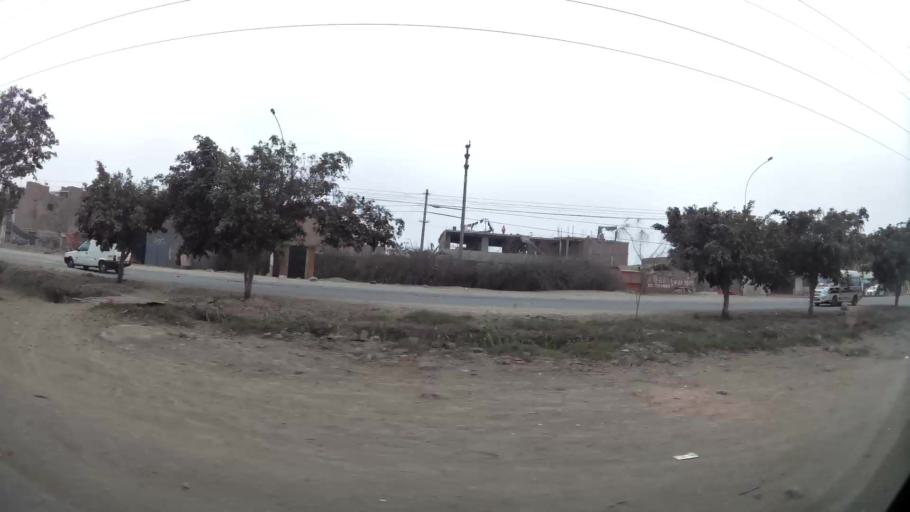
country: PE
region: Lima
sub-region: Lima
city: Urb. Santo Domingo
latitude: -11.8953
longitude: -77.0475
